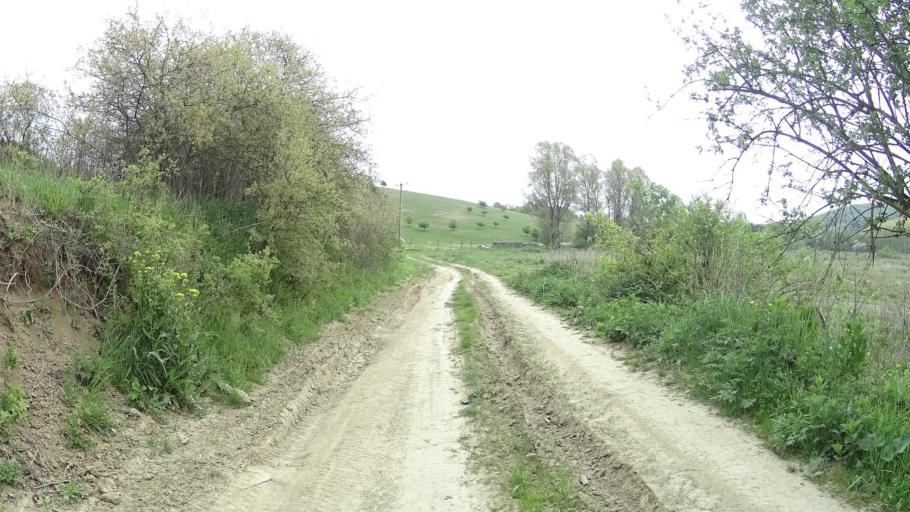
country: HU
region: Nograd
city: Romhany
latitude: 47.8736
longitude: 19.2362
